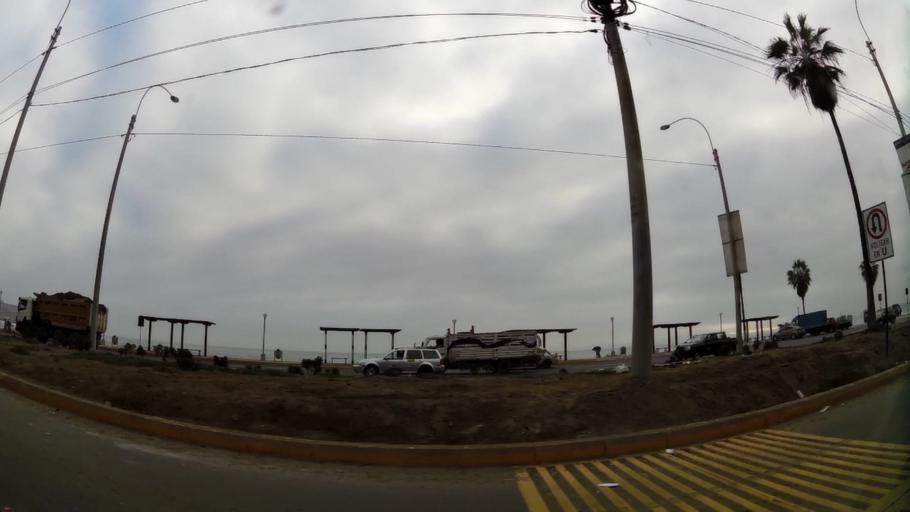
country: PE
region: Lima
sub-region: Lima
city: Surco
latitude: -12.1462
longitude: -77.0252
